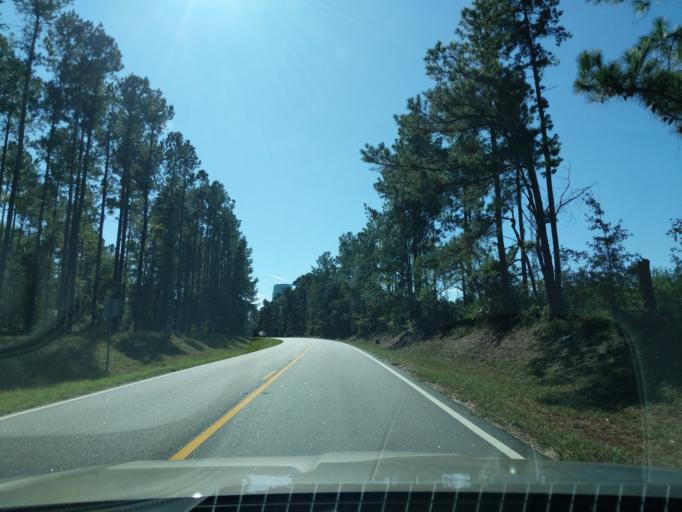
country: US
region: Georgia
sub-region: Richmond County
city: Hephzibah
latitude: 33.2765
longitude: -82.0150
